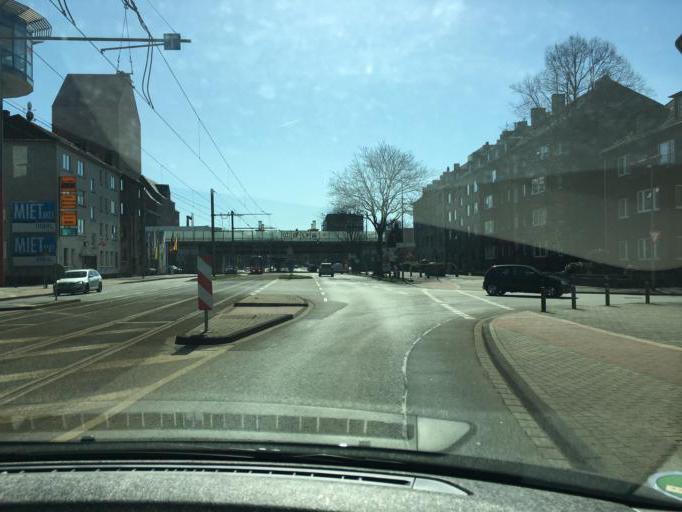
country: DE
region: North Rhine-Westphalia
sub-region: Regierungsbezirk Dusseldorf
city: Duisburg
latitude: 51.4384
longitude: 6.7552
